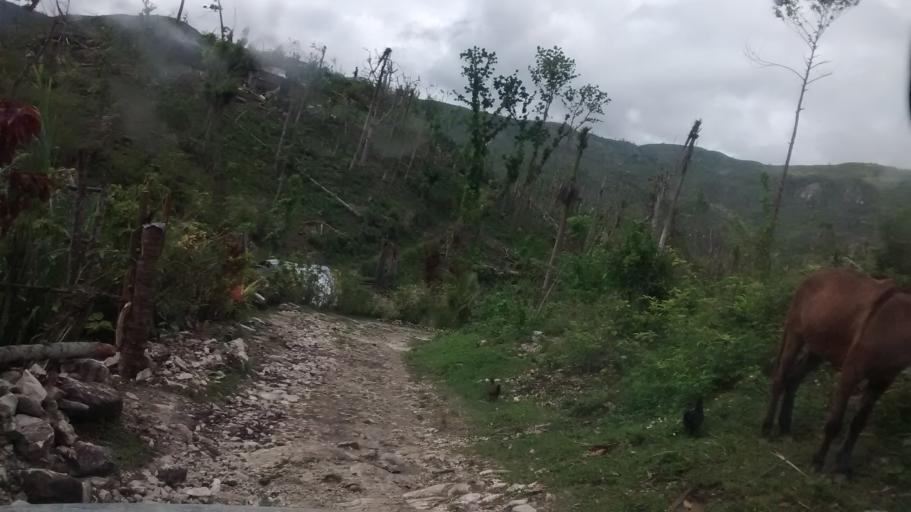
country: HT
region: Grandans
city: Moron
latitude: 18.5591
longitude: -74.2707
